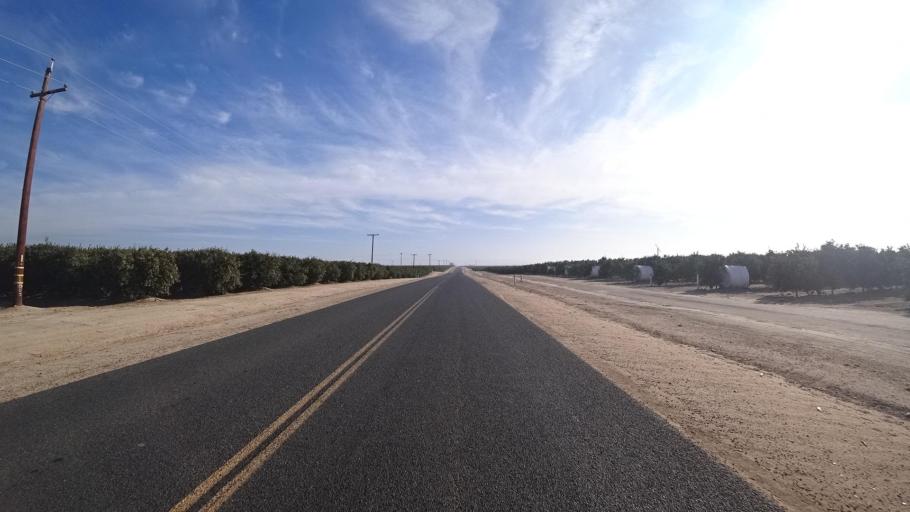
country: US
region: California
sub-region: Kern County
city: McFarland
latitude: 35.6022
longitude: -119.1267
